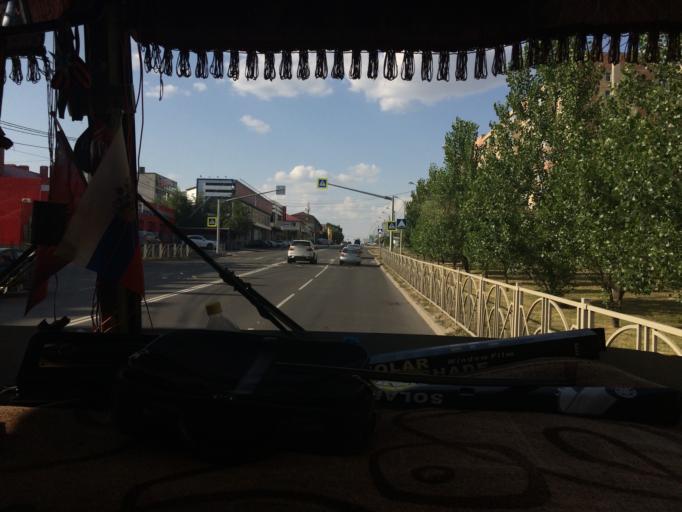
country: RU
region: Stavropol'skiy
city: Tatarka
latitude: 45.0029
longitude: 41.9114
